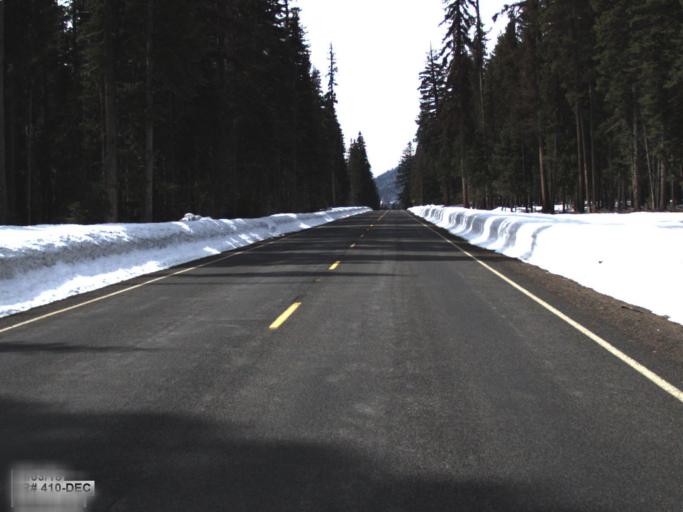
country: US
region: Washington
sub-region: Kittitas County
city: Cle Elum
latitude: 46.9534
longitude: -121.3020
